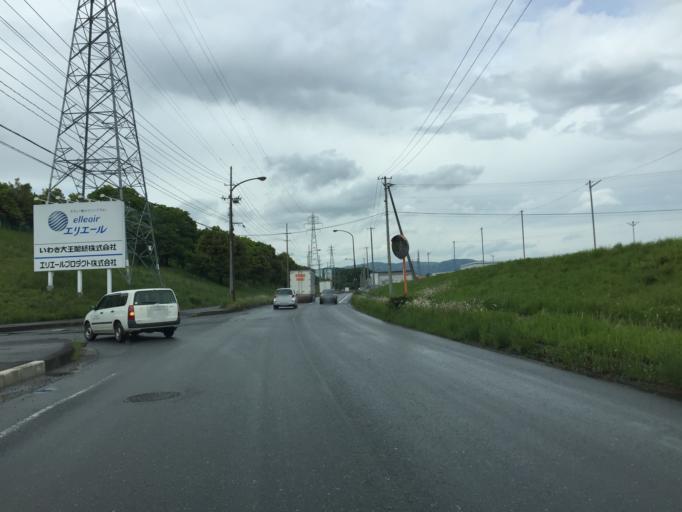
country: JP
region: Ibaraki
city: Kitaibaraki
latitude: 36.9350
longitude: 140.7470
